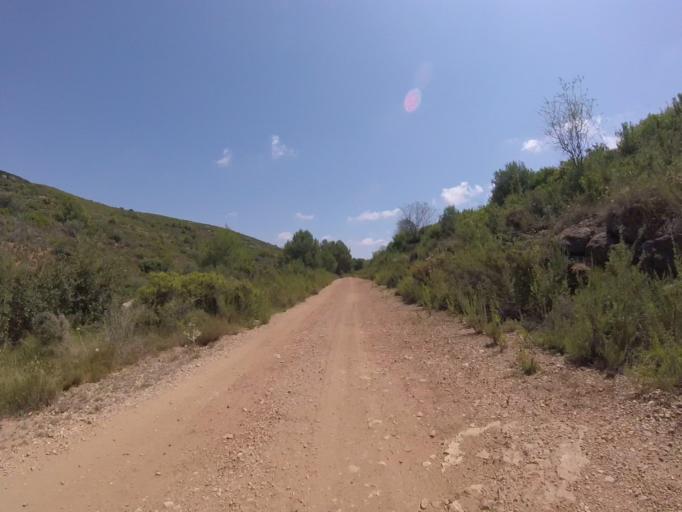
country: ES
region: Valencia
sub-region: Provincia de Castello
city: Torreblanca
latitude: 40.2224
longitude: 0.1487
